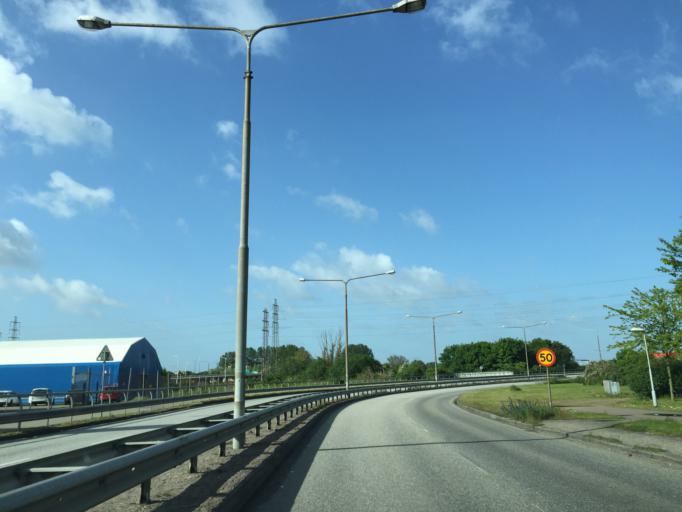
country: SE
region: Skane
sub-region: Burlovs Kommun
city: Arloev
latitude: 55.6238
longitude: 13.0614
